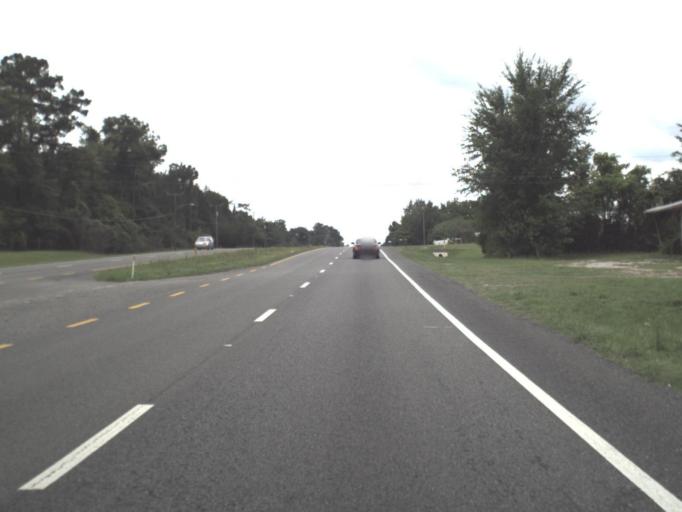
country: US
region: Florida
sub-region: Nassau County
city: Hilliard
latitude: 30.7029
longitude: -81.9261
